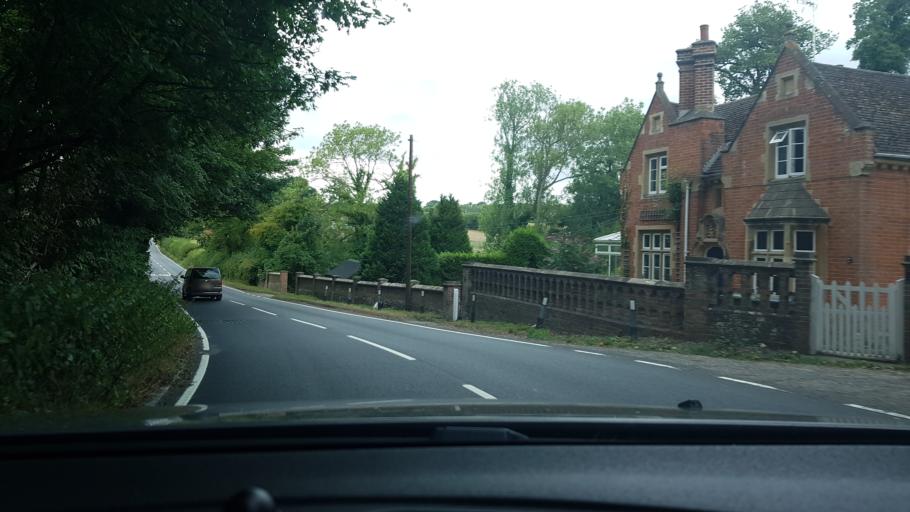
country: GB
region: England
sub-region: West Berkshire
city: Theale
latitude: 51.4435
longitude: -1.1165
